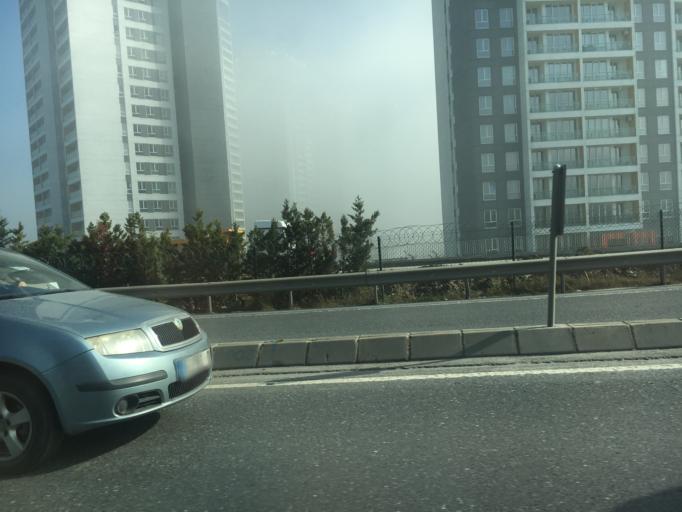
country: TR
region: Istanbul
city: Esenyurt
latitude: 41.0532
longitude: 28.6845
